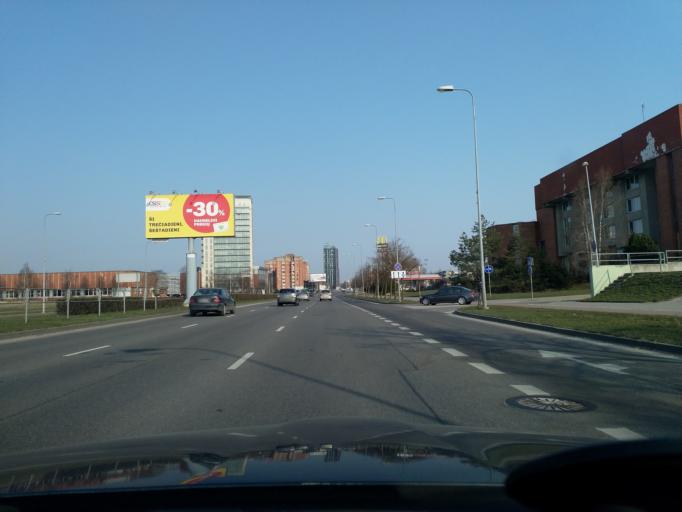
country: LT
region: Klaipedos apskritis
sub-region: Klaipeda
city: Klaipeda
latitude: 55.6905
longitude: 21.1549
